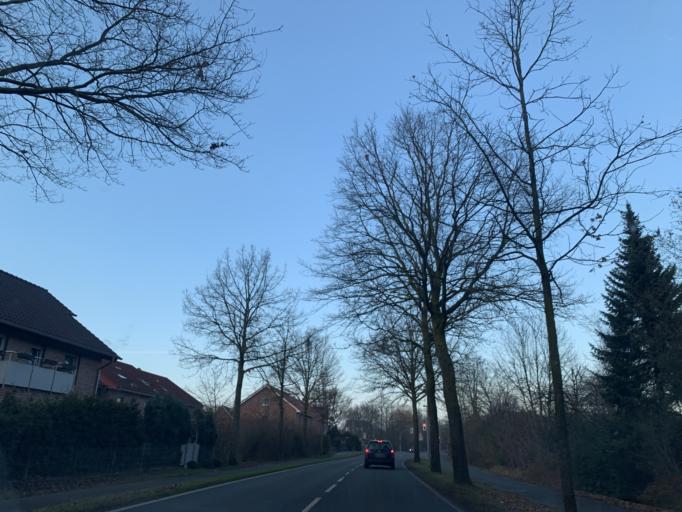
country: DE
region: North Rhine-Westphalia
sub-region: Regierungsbezirk Munster
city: Muenster
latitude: 51.9049
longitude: 7.6250
